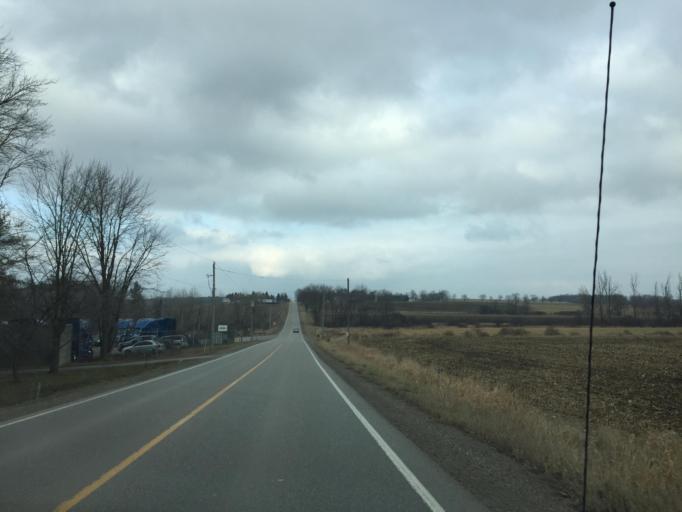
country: CA
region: Ontario
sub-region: Wellington County
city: Guelph
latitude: 43.5124
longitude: -80.3317
